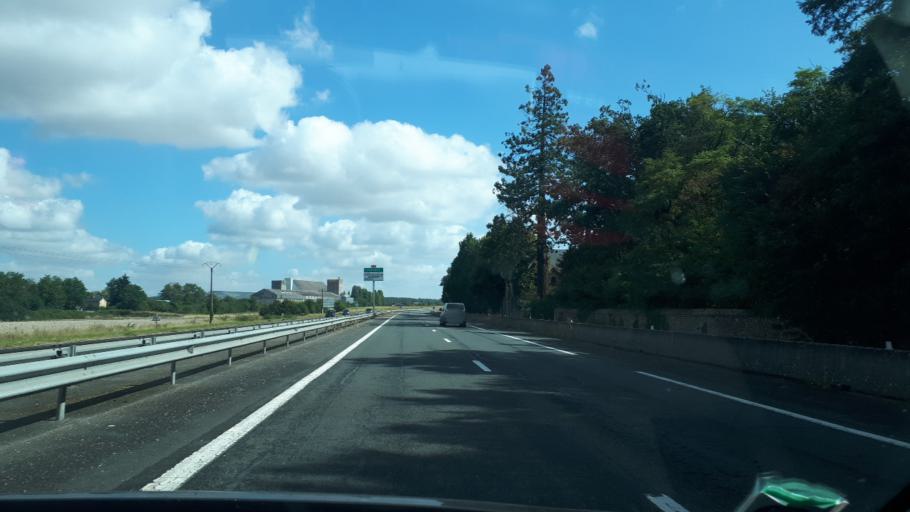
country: FR
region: Centre
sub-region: Departement du Loir-et-Cher
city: Saint-Ouen
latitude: 47.8414
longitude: 1.0911
